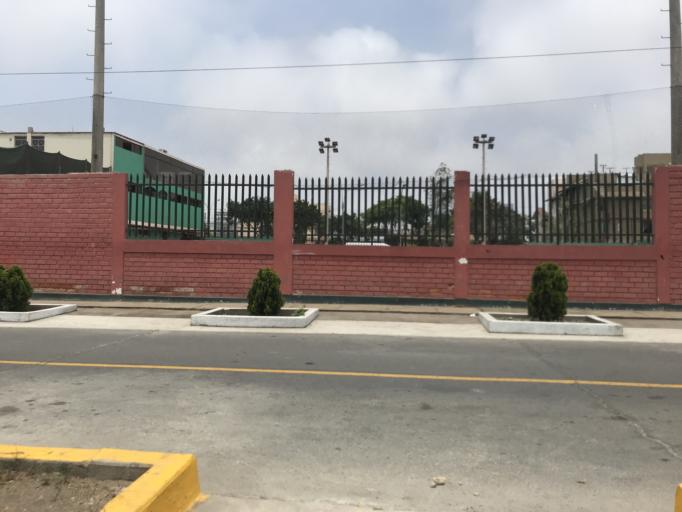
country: PE
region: Lima
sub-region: Lima
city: San Isidro
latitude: -12.0835
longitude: -77.0764
